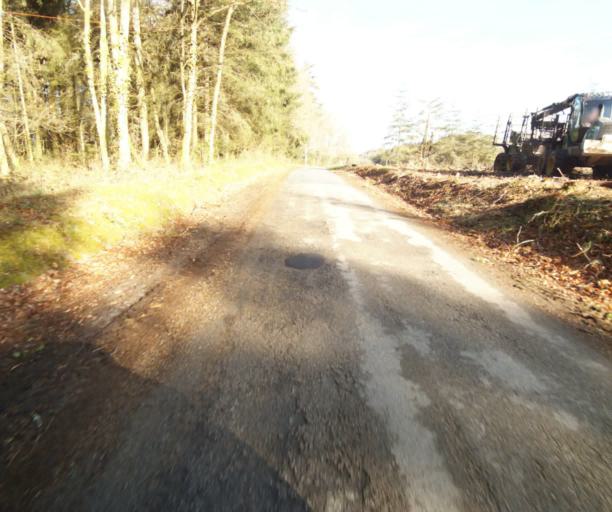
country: FR
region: Limousin
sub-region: Departement de la Correze
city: Correze
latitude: 45.2799
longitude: 1.8709
